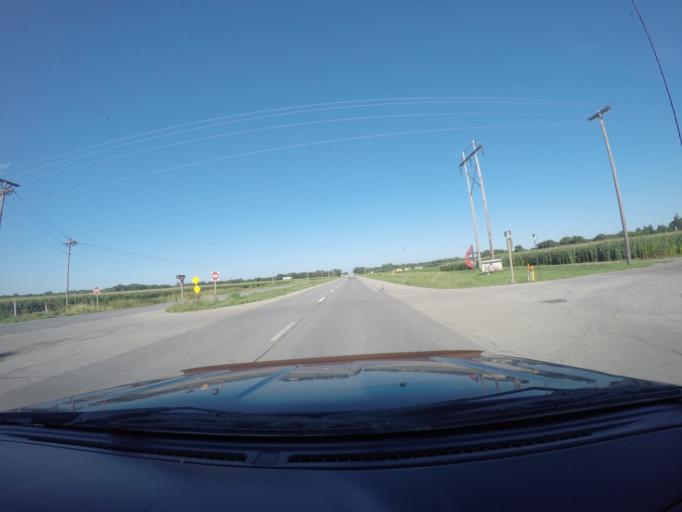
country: US
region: Kansas
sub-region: Shawnee County
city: Topeka
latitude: 39.0876
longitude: -95.5670
